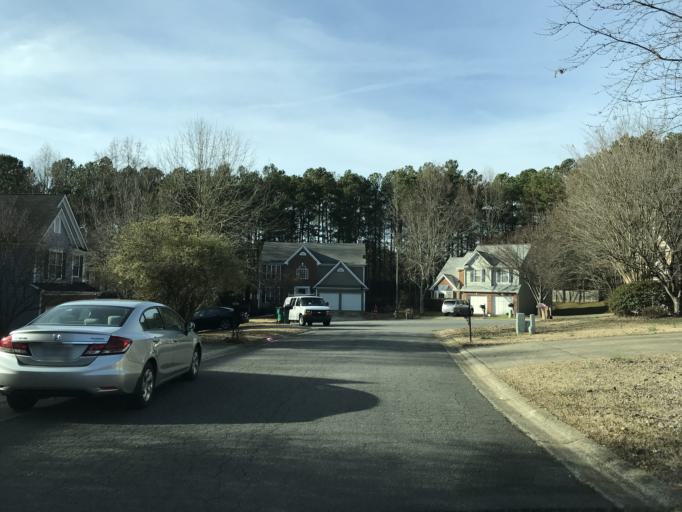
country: US
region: Georgia
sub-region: Cobb County
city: Kennesaw
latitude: 34.0585
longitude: -84.5977
